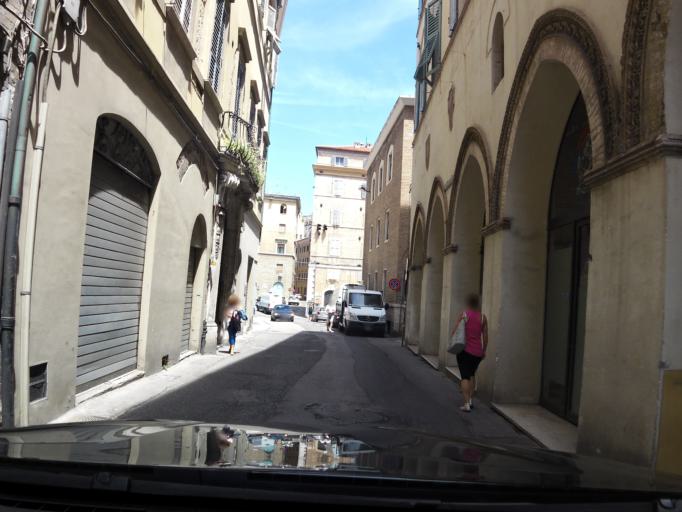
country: IT
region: The Marches
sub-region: Provincia di Ancona
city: Le Grazie di Ancona
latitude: 43.6202
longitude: 13.5100
